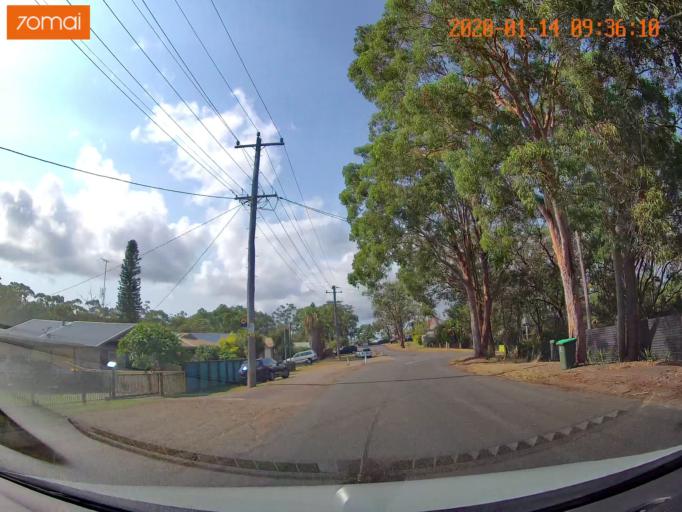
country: AU
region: New South Wales
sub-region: Lake Macquarie Shire
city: Arcadia vale
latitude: -33.1099
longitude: 151.5561
